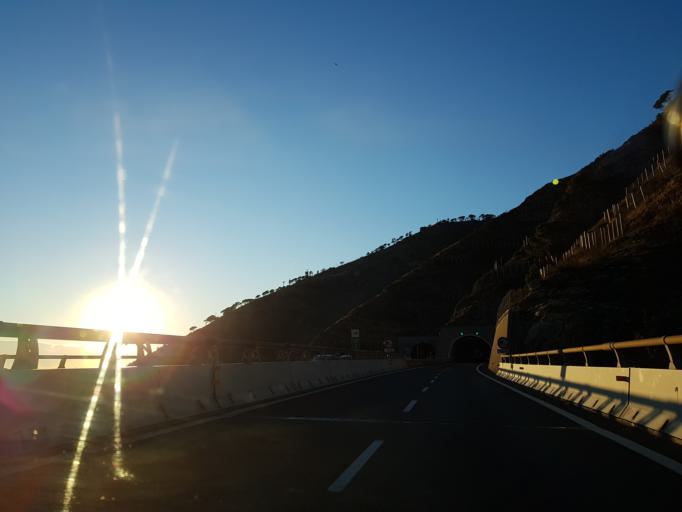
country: IT
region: Liguria
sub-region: Provincia di Genova
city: Bogliasco
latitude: 44.3924
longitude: 9.0403
